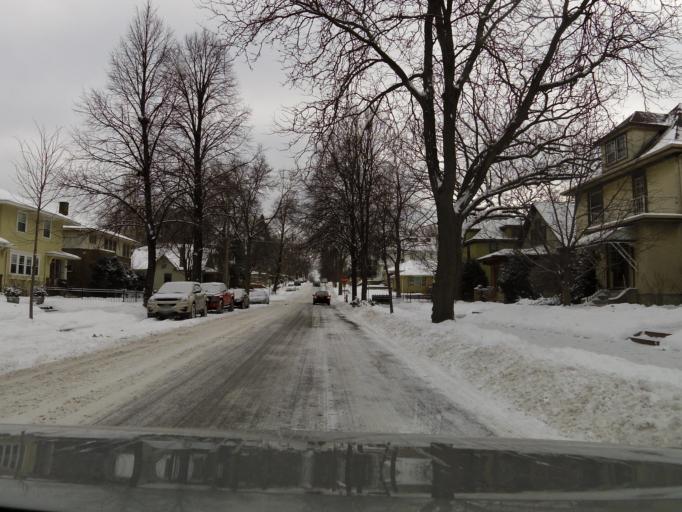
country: US
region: Minnesota
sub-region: Hennepin County
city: Saint Louis Park
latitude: 44.9419
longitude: -93.3009
